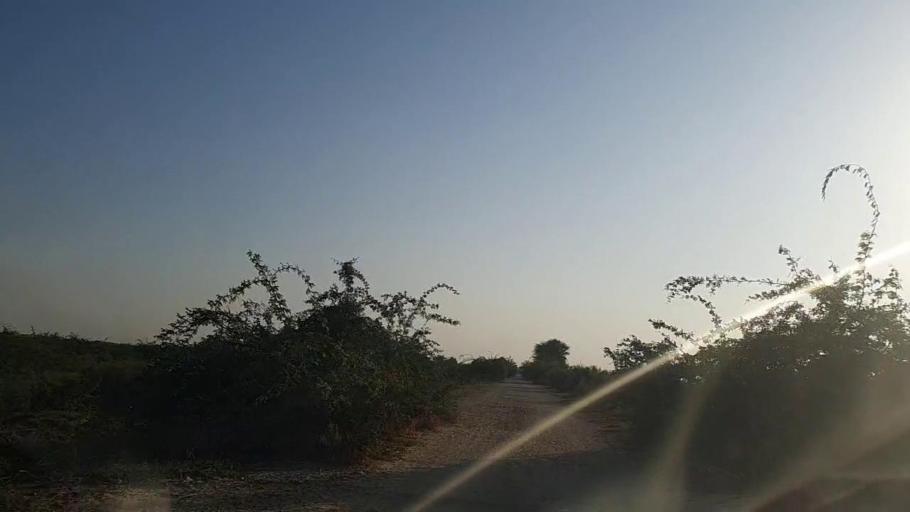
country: PK
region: Sindh
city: Jati
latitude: 24.4255
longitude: 68.1883
